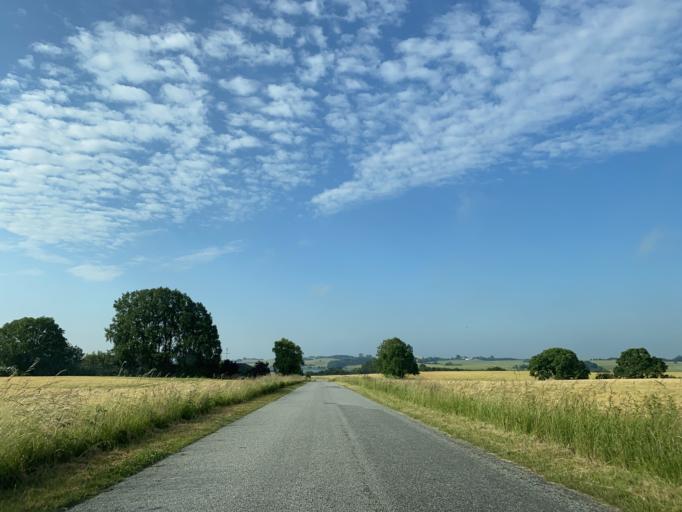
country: DK
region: South Denmark
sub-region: Haderslev Kommune
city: Haderslev
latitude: 55.1790
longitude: 9.4816
